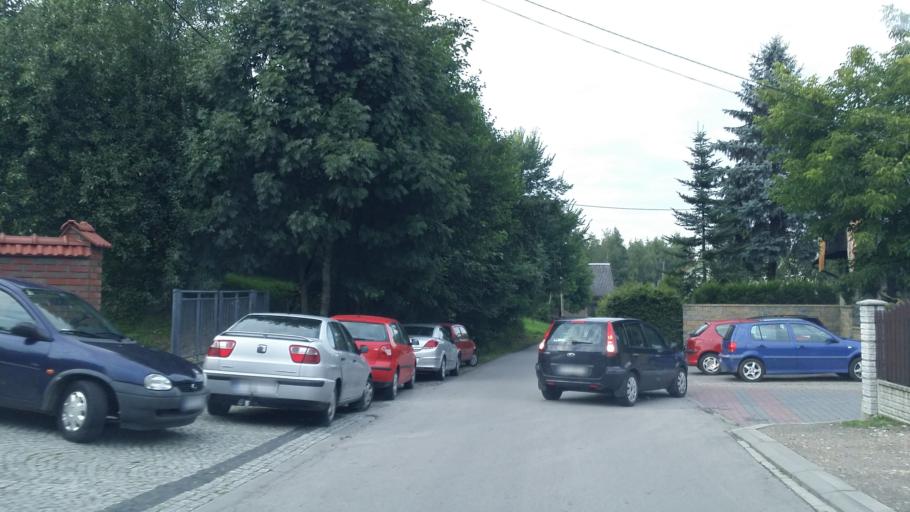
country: PL
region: Lesser Poland Voivodeship
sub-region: Powiat wadowicki
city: Spytkowice
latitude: 49.9883
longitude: 19.5024
